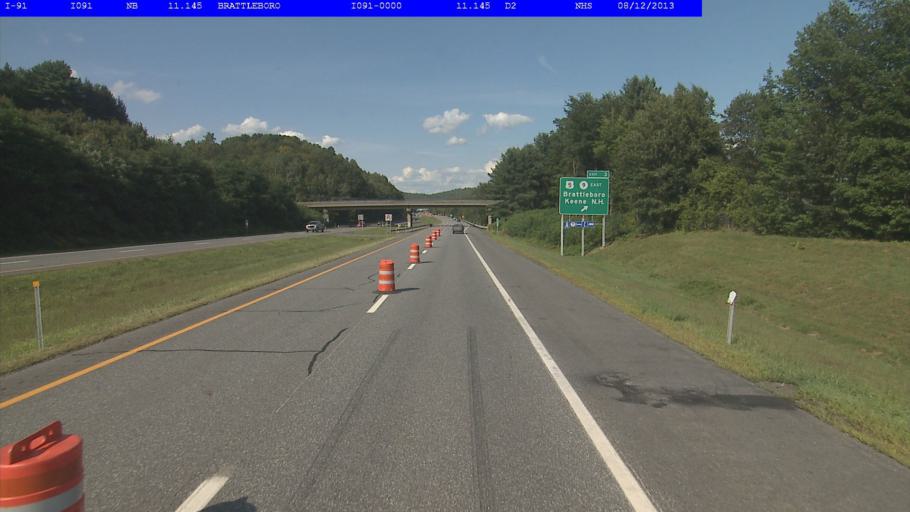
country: US
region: Vermont
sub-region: Windham County
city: Brattleboro
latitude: 42.8809
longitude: -72.5634
